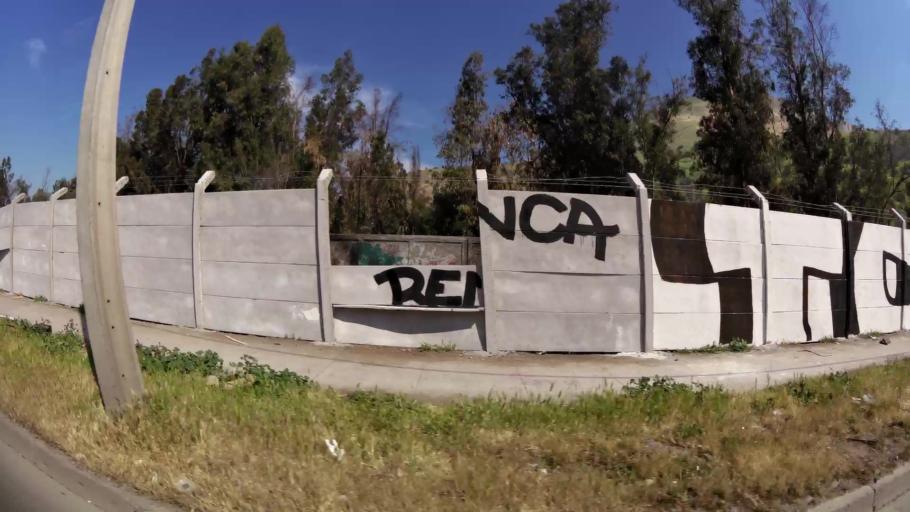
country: CL
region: Santiago Metropolitan
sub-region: Provincia de Santiago
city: Lo Prado
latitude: -33.3945
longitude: -70.7015
